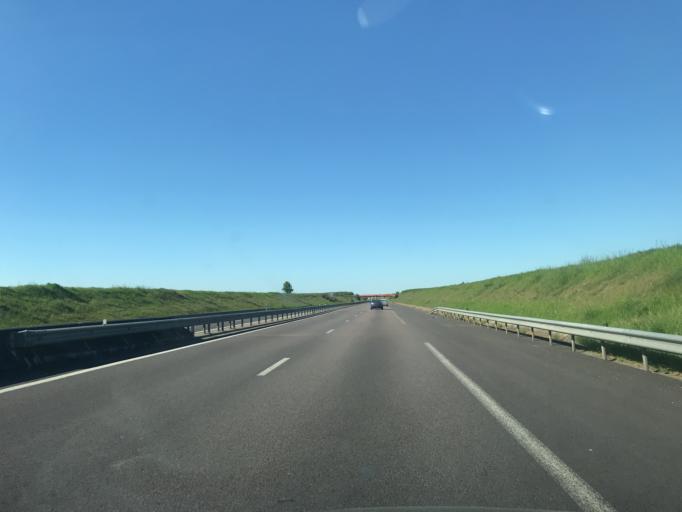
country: FR
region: Haute-Normandie
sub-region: Departement de l'Eure
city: Evreux
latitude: 48.9654
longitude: 1.1985
